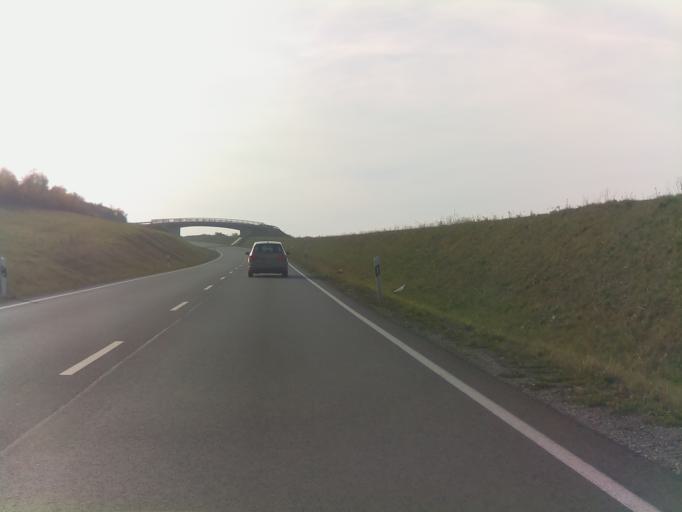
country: DE
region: Baden-Wuerttemberg
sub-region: Regierungsbezirk Stuttgart
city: Igersheim
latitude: 49.4844
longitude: 9.7959
